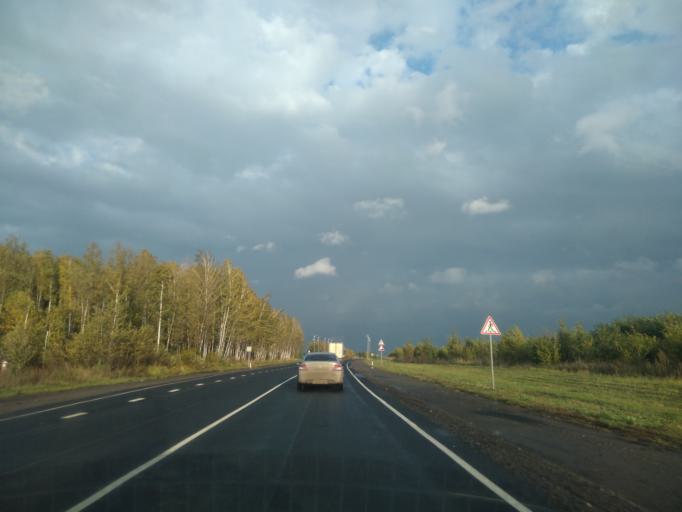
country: RU
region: Lipetsk
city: Donskoye
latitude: 52.5860
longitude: 38.8257
